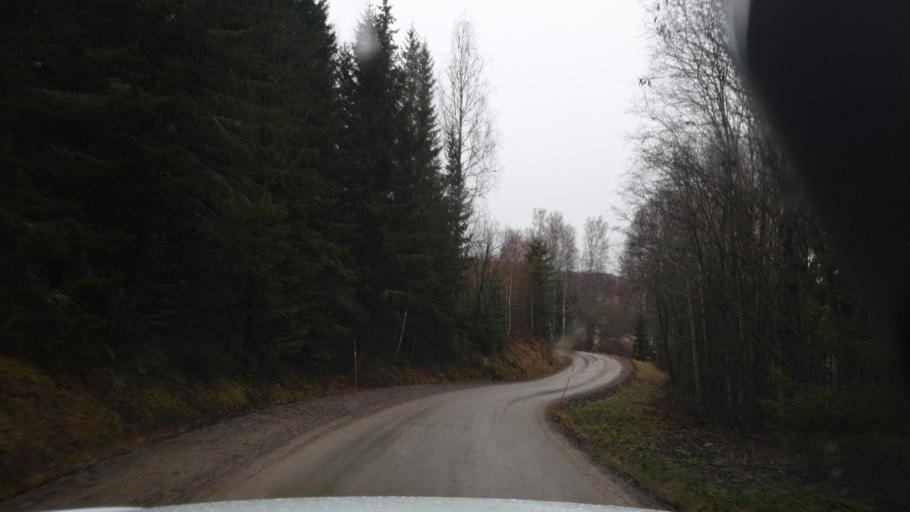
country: SE
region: Vaermland
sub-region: Arvika Kommun
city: Arvika
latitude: 59.6626
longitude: 12.7603
